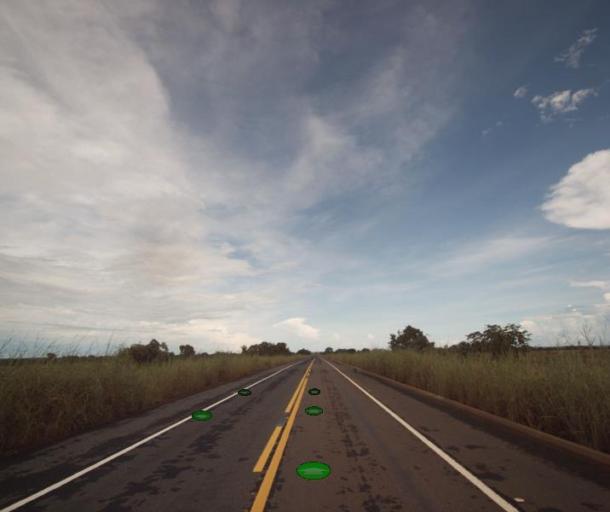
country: BR
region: Goias
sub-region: Sao Miguel Do Araguaia
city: Sao Miguel do Araguaia
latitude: -13.2768
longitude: -50.4996
